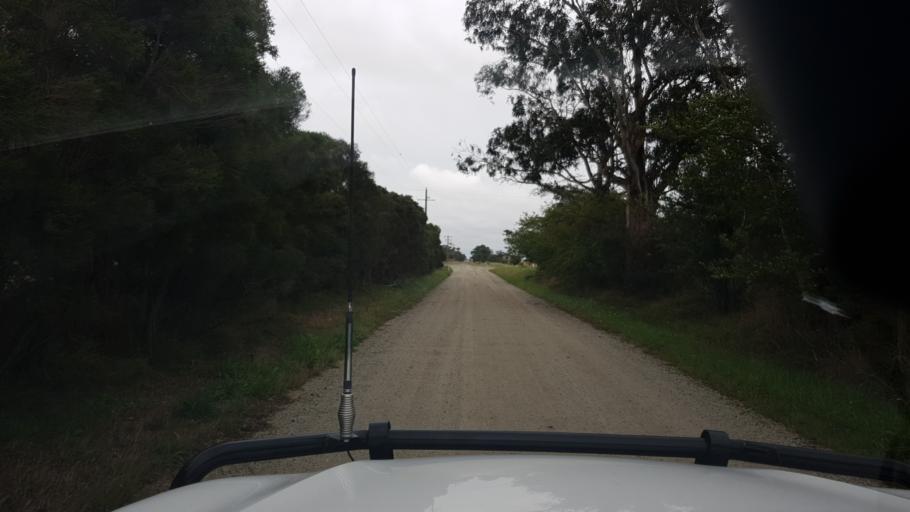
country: AU
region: Victoria
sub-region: Cardinia
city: Bunyip
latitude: -38.1593
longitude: 145.7082
